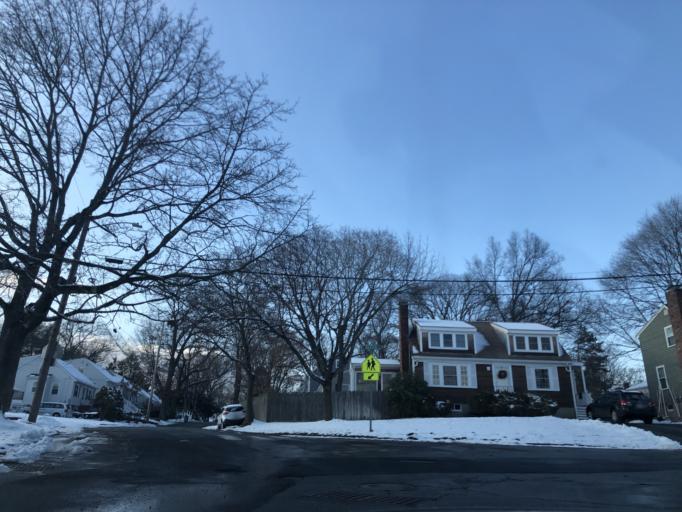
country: US
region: Massachusetts
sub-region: Middlesex County
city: Arlington
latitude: 42.4269
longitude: -71.1661
